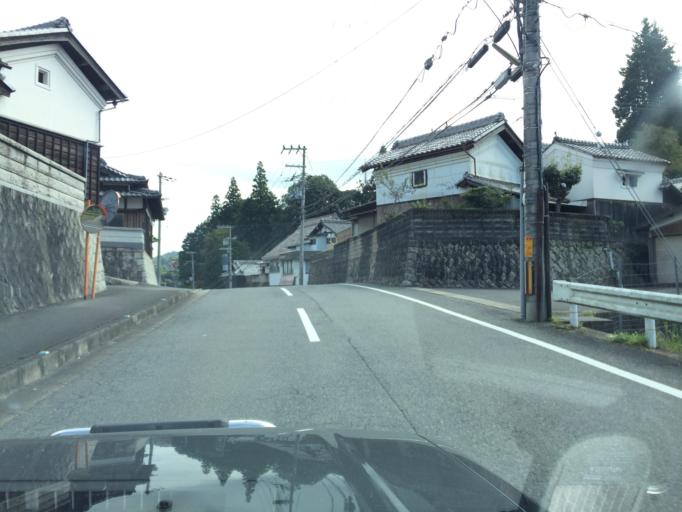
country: JP
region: Mie
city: Nabari
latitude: 34.6809
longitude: 136.0401
